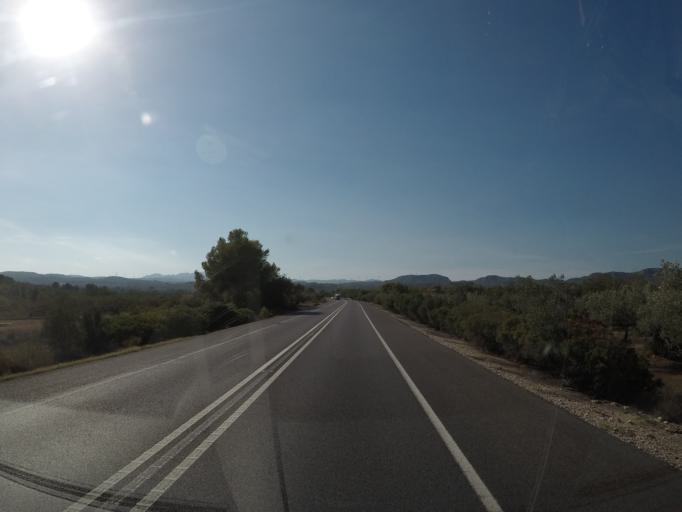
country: ES
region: Catalonia
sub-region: Provincia de Tarragona
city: El Perello
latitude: 40.8973
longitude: 0.7385
